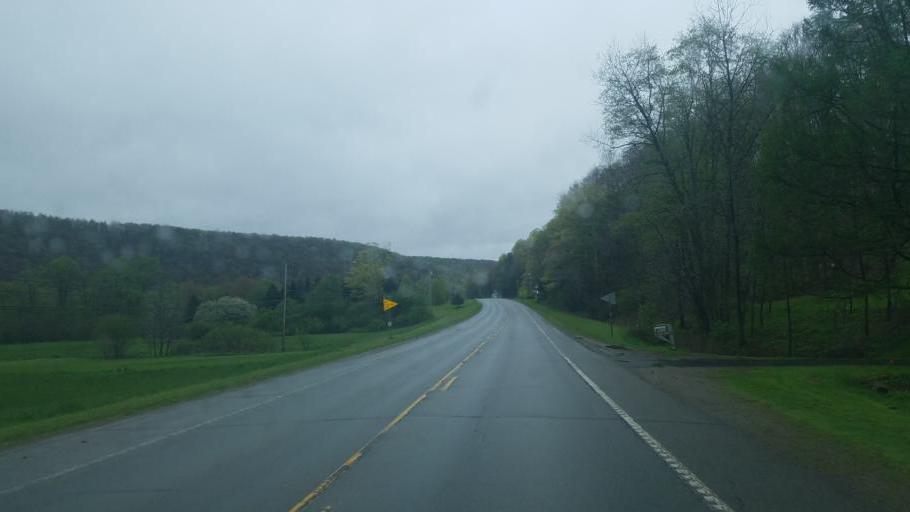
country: US
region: Pennsylvania
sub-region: Potter County
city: Coudersport
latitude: 41.8058
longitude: -78.0173
